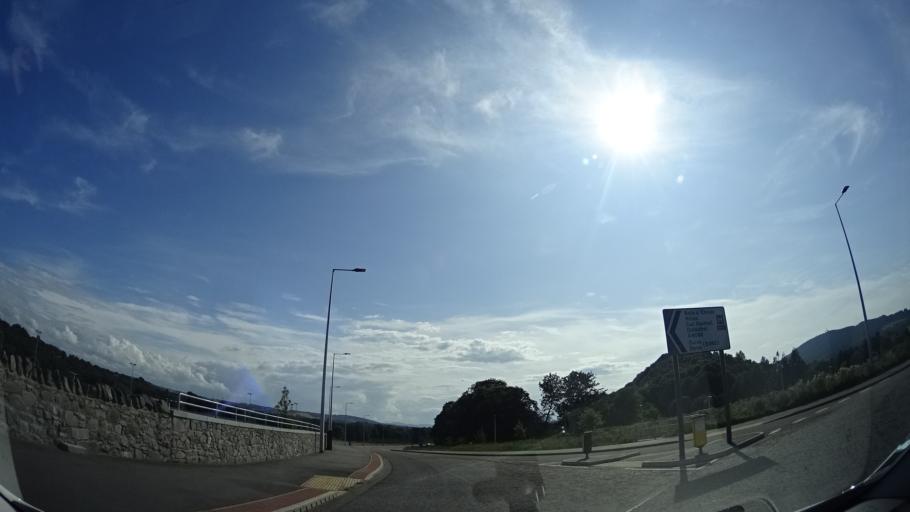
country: GB
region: Scotland
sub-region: Highland
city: Inverness
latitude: 57.4633
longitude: -4.2424
